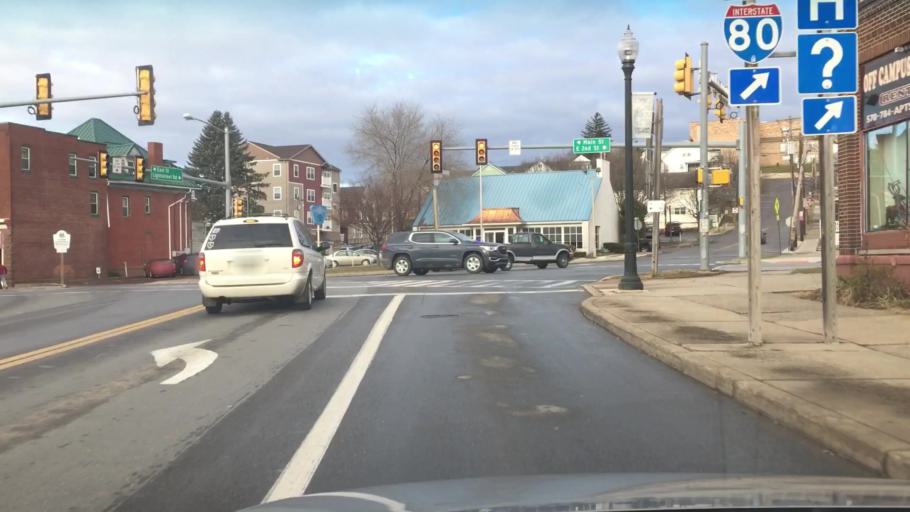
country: US
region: Pennsylvania
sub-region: Columbia County
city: Bloomsburg
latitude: 41.0043
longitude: -76.4534
